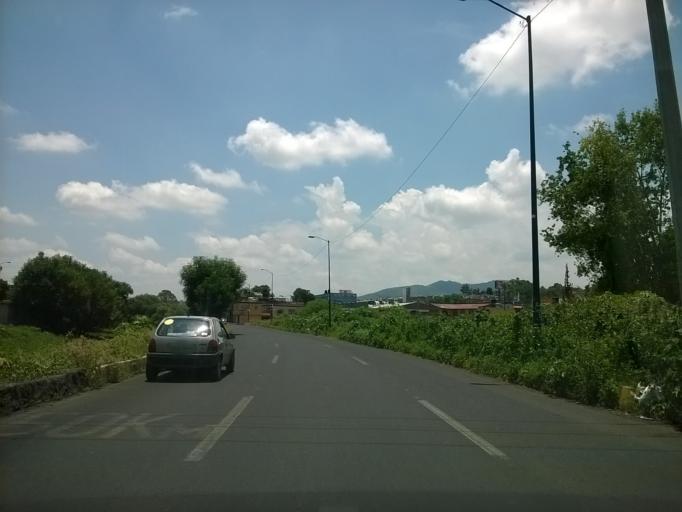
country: MX
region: Michoacan
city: Morelia
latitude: 19.7119
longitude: -101.1911
